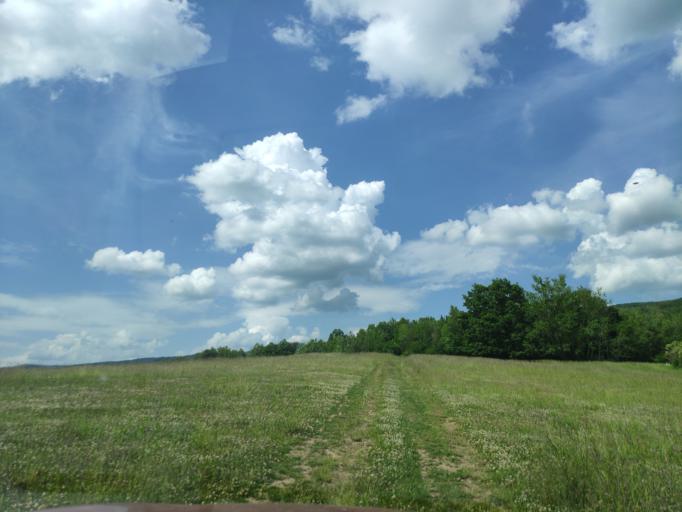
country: SK
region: Kosicky
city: Medzev
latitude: 48.7185
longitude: 20.9622
